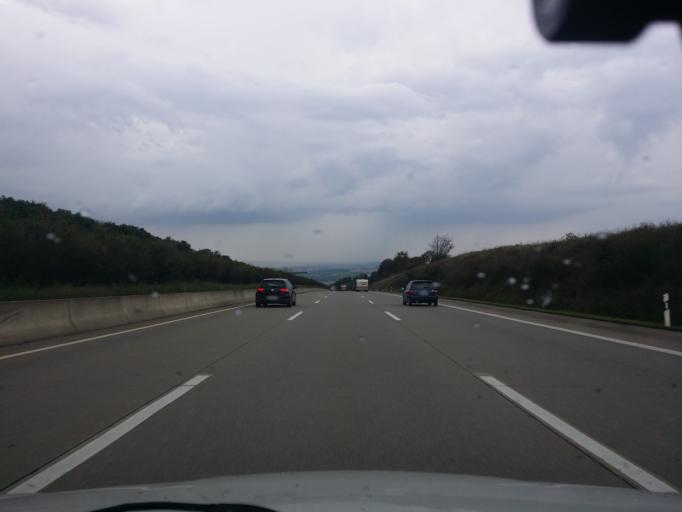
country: DE
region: Thuringia
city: Mellingen
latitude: 50.9175
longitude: 11.4091
